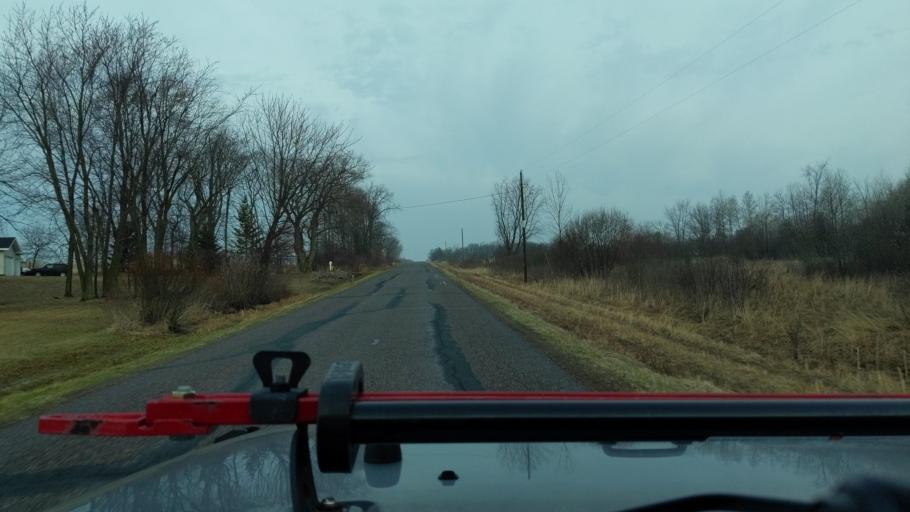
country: US
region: Wisconsin
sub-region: Saint Croix County
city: Hammond
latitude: 44.9344
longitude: -92.4291
